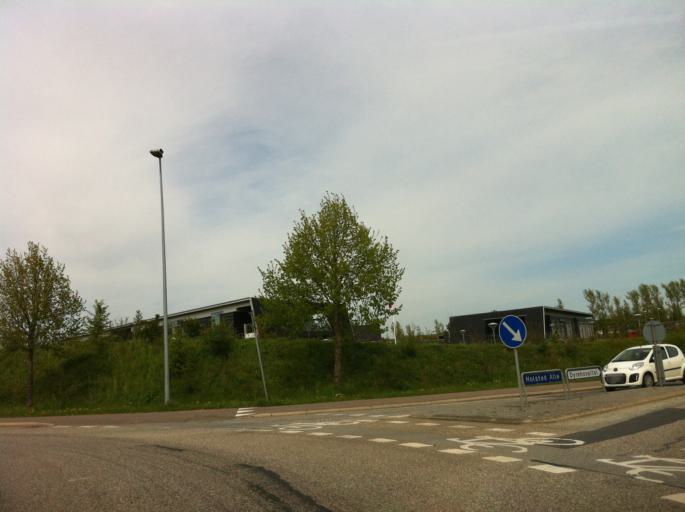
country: DK
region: Zealand
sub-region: Naestved Kommune
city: Naestved
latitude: 55.2572
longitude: 11.7550
